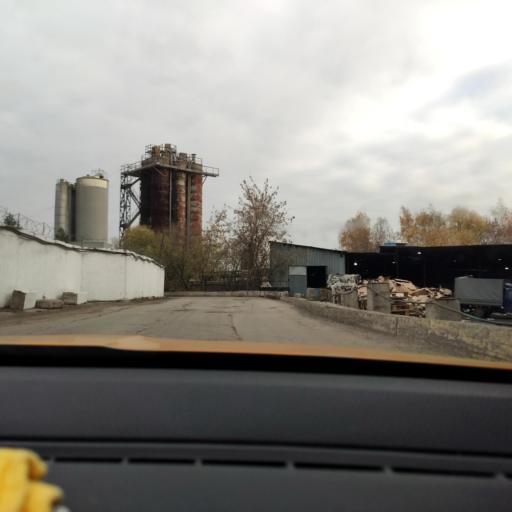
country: RU
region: Moscow
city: Ochakovo-Matveyevskoye
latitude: 55.7027
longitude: 37.4388
